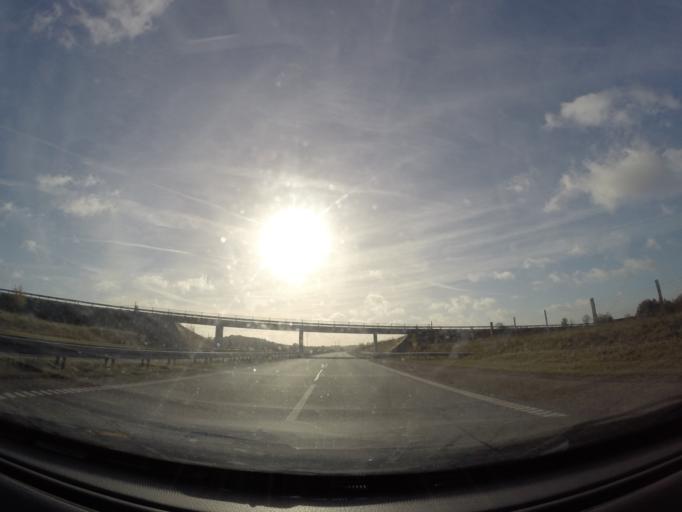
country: DK
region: South Denmark
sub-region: Svendborg Kommune
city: Svendborg
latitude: 55.1286
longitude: 10.5612
